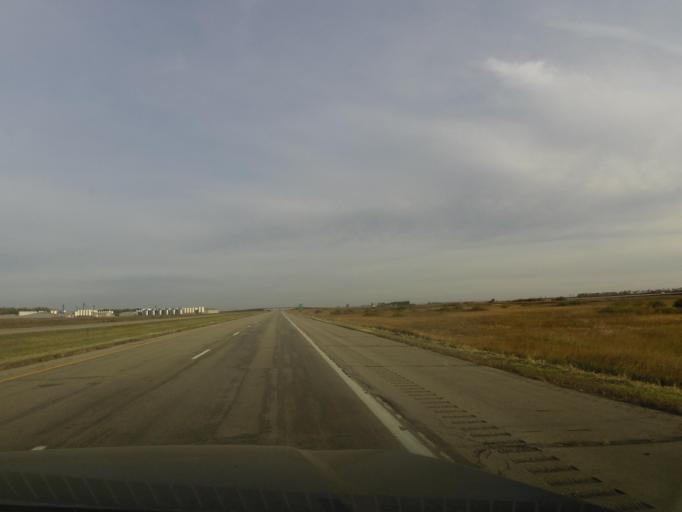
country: US
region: Minnesota
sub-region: Kittson County
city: Hallock
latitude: 48.7933
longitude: -97.2298
